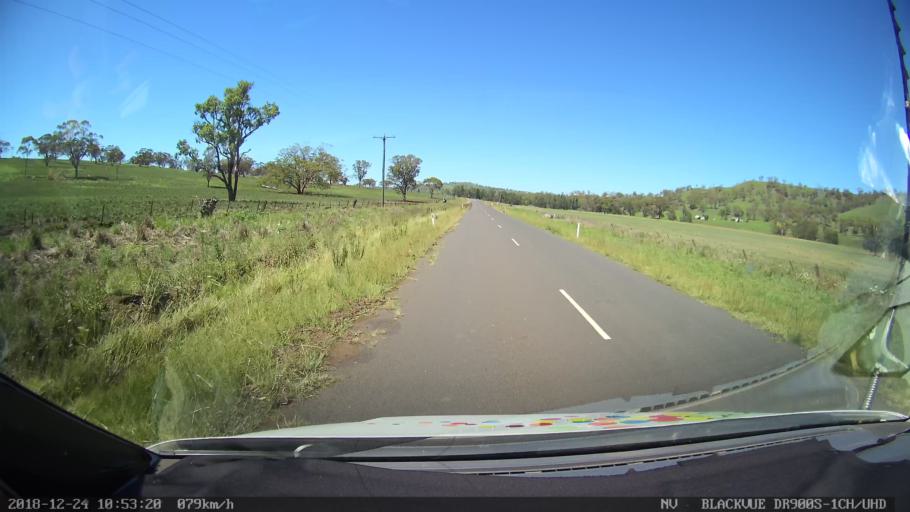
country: AU
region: New South Wales
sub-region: Upper Hunter Shire
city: Merriwa
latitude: -31.9905
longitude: 150.4216
